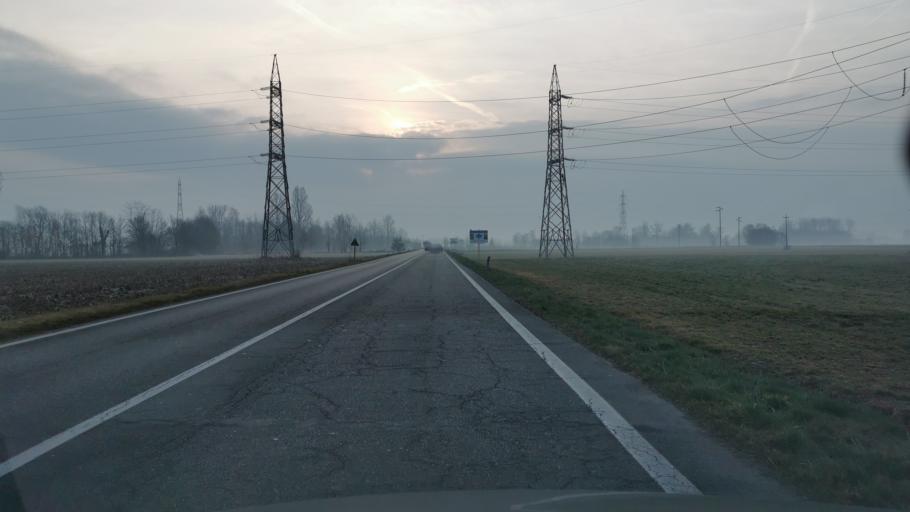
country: IT
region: Piedmont
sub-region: Provincia di Torino
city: Ciconio
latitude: 45.3411
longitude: 7.7735
